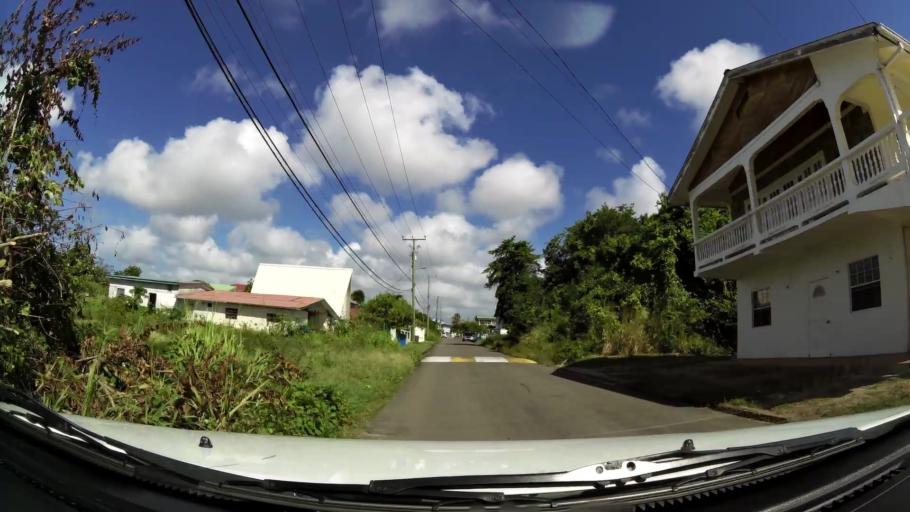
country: LC
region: Laborie Quarter
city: Laborie
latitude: 13.7419
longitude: -60.9764
